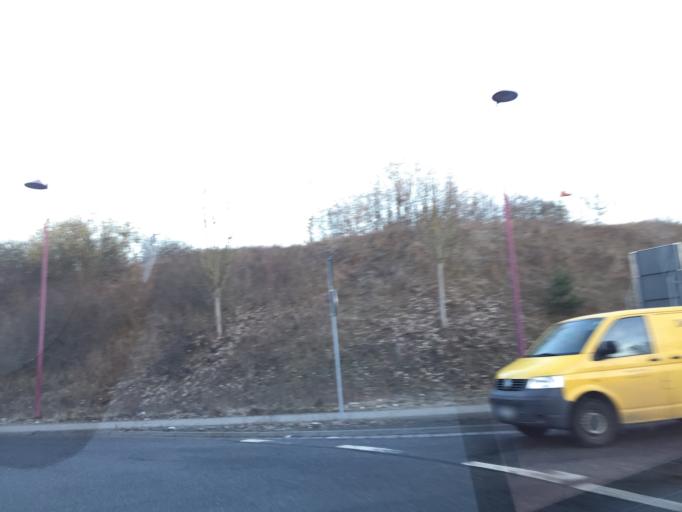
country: DE
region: Rheinland-Pfalz
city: Montabaur
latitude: 50.4468
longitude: 7.8307
